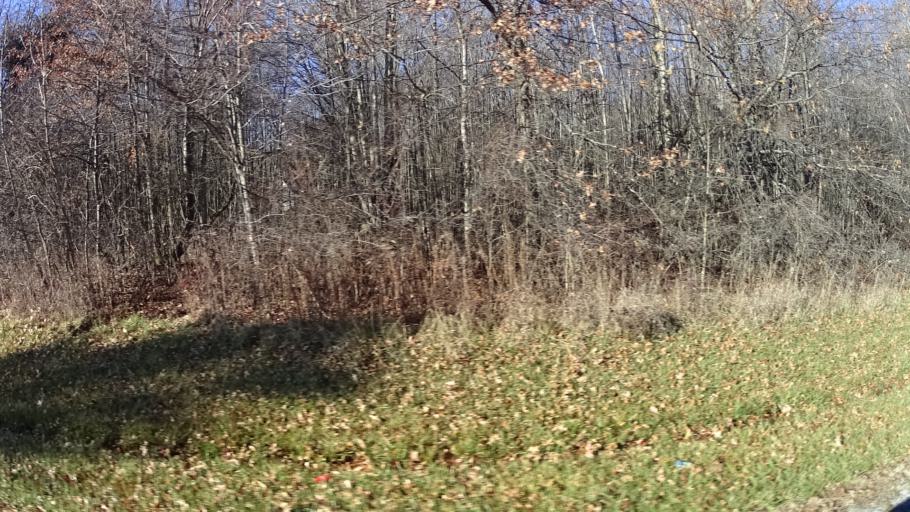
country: US
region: Ohio
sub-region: Lorain County
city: Wellington
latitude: 41.1112
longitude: -82.1806
